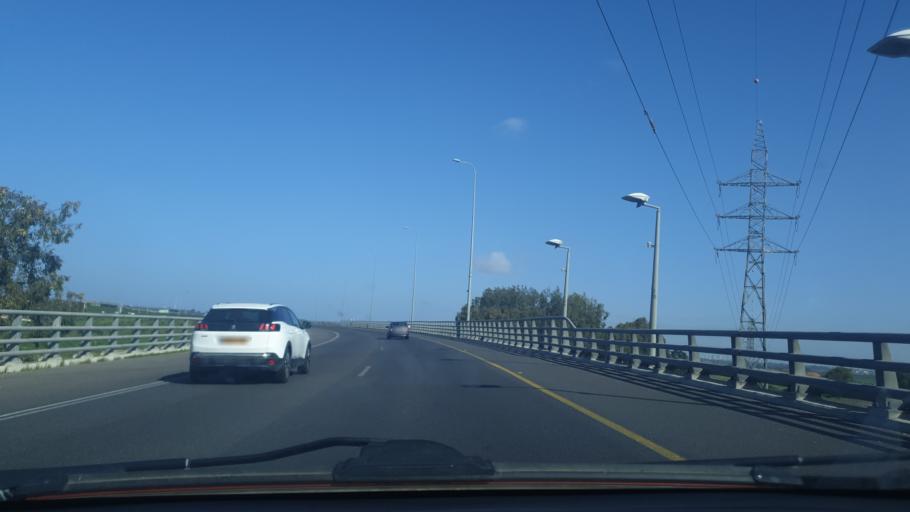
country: IL
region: Tel Aviv
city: Kefar Shemaryahu
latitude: 32.2141
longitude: 34.8395
